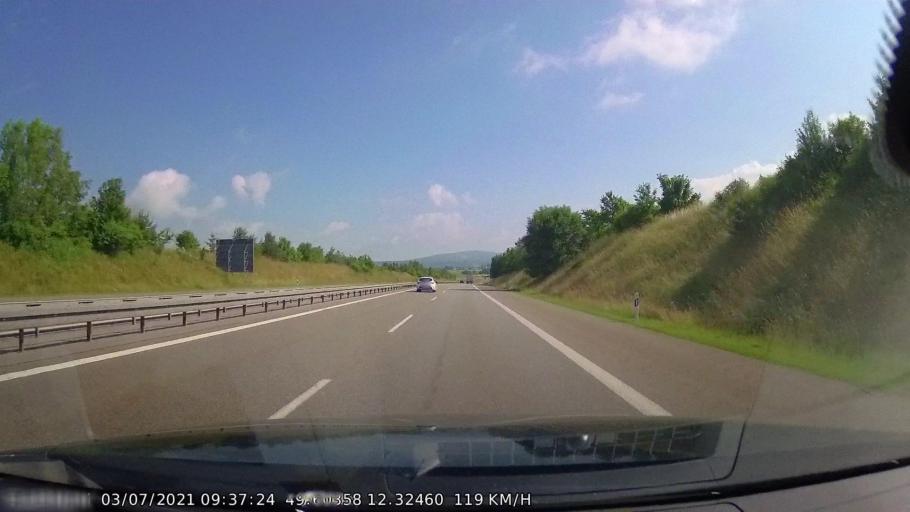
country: DE
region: Bavaria
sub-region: Upper Palatinate
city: Vohenstrauss
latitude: 49.6036
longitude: 12.3247
